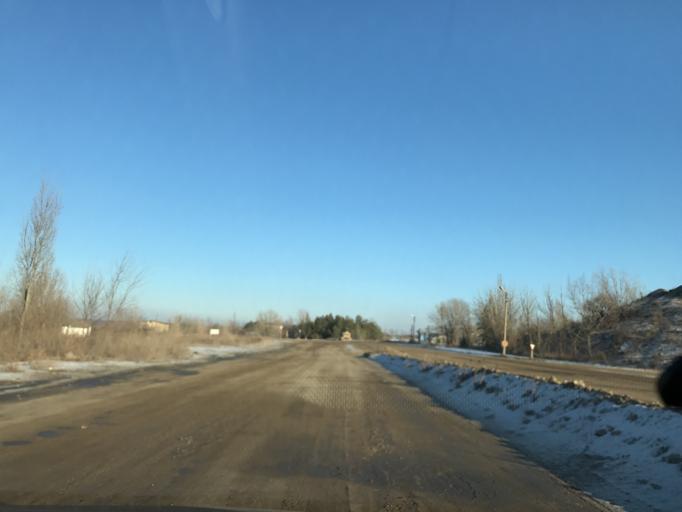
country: RU
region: Rostov
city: Staraya Stanitsa
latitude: 48.2375
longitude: 40.4029
